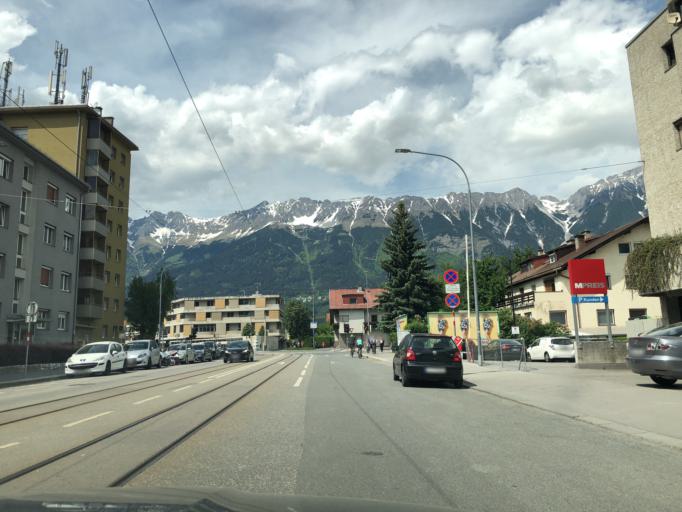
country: AT
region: Tyrol
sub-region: Innsbruck Stadt
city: Innsbruck
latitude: 47.2600
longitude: 11.4206
